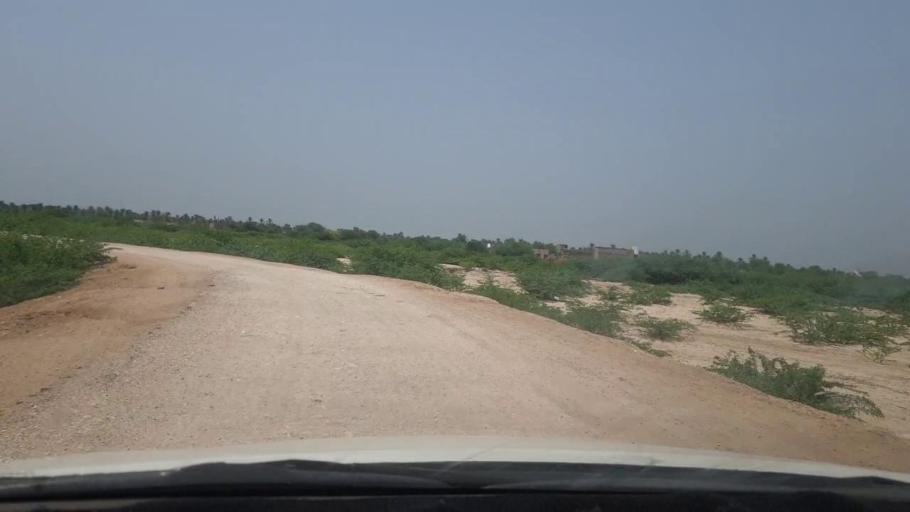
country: PK
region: Sindh
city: Khairpur
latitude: 27.5006
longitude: 68.8861
